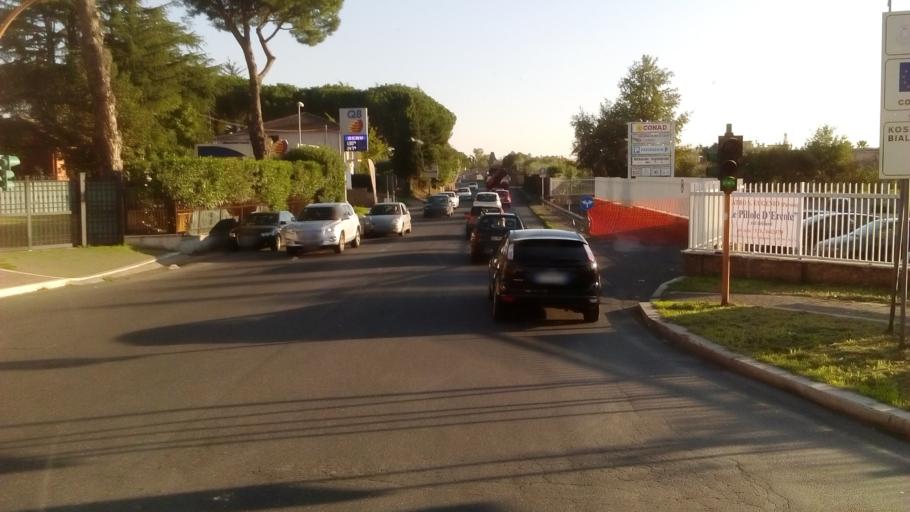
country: IT
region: Latium
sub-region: Citta metropolitana di Roma Capitale
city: Pavona
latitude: 41.7256
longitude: 12.6180
